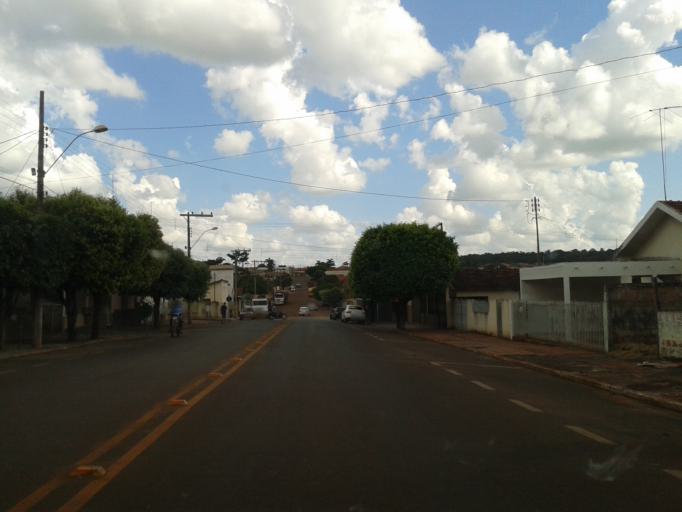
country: BR
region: Minas Gerais
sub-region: Capinopolis
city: Capinopolis
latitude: -18.6828
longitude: -49.5743
